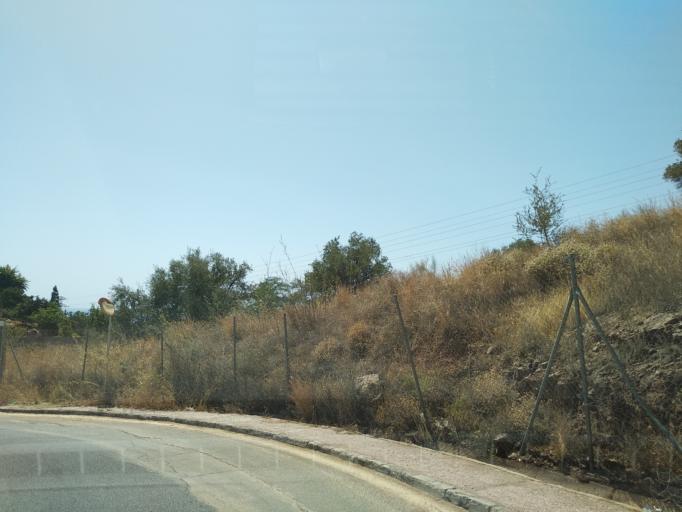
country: ES
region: Andalusia
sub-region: Provincia de Malaga
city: Malaga
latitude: 36.7329
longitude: -4.3862
